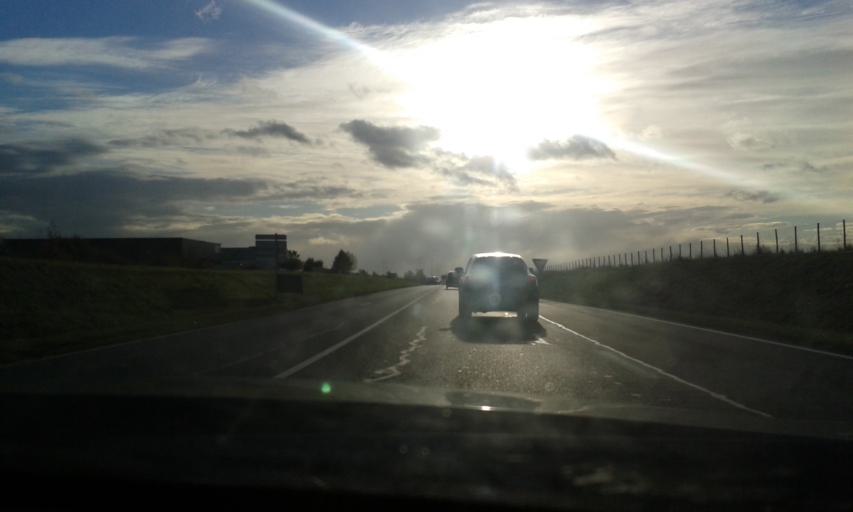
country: FR
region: Centre
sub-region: Departement d'Eure-et-Loir
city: Mainvilliers
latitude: 48.4495
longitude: 1.4421
